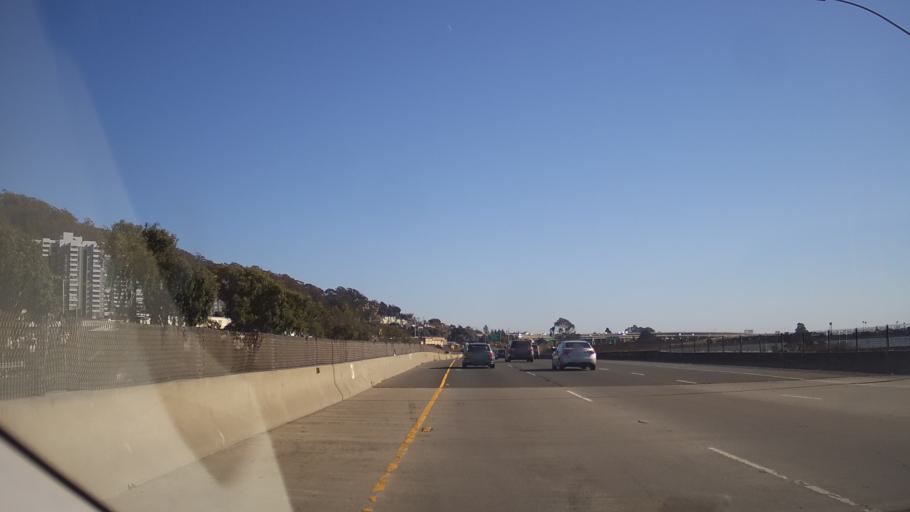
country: US
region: California
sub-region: Alameda County
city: Albany
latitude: 37.8971
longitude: -122.3117
